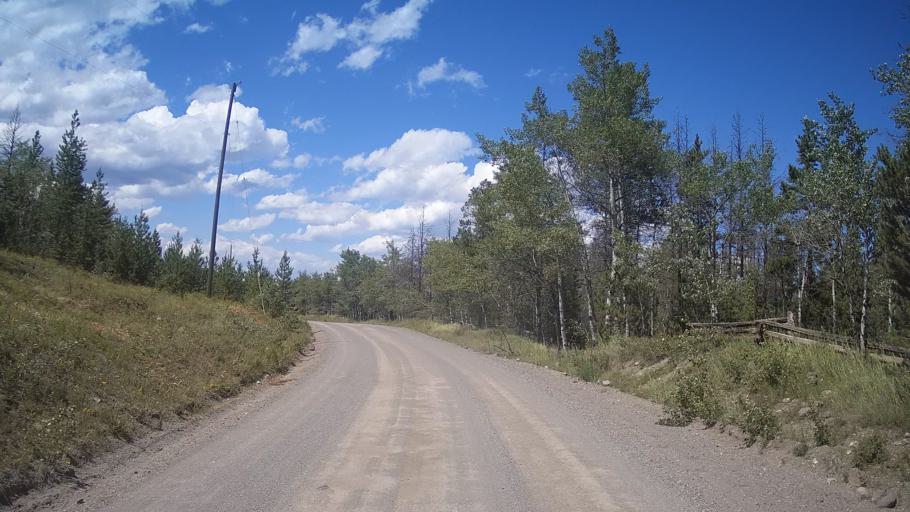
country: CA
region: British Columbia
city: Cache Creek
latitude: 51.2495
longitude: -121.6646
